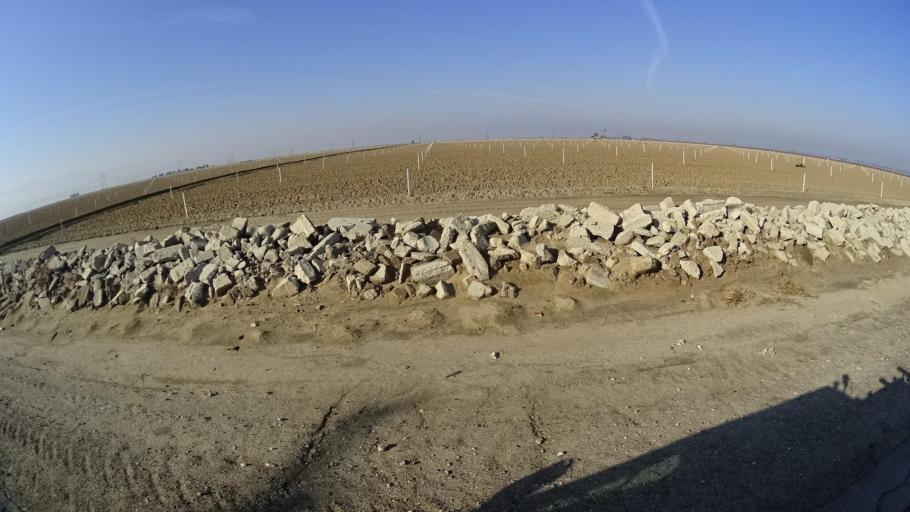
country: US
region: California
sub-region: Kern County
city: Weedpatch
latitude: 35.1334
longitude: -118.9677
